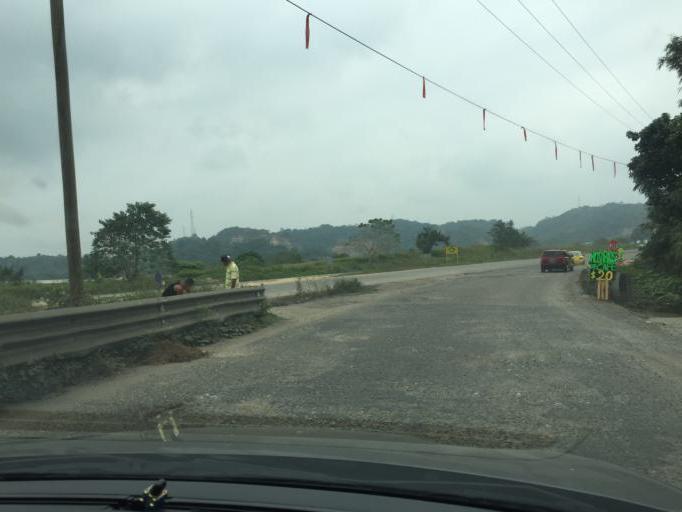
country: MX
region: Veracruz
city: Villa Nanchital
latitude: 18.0735
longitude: -94.3185
